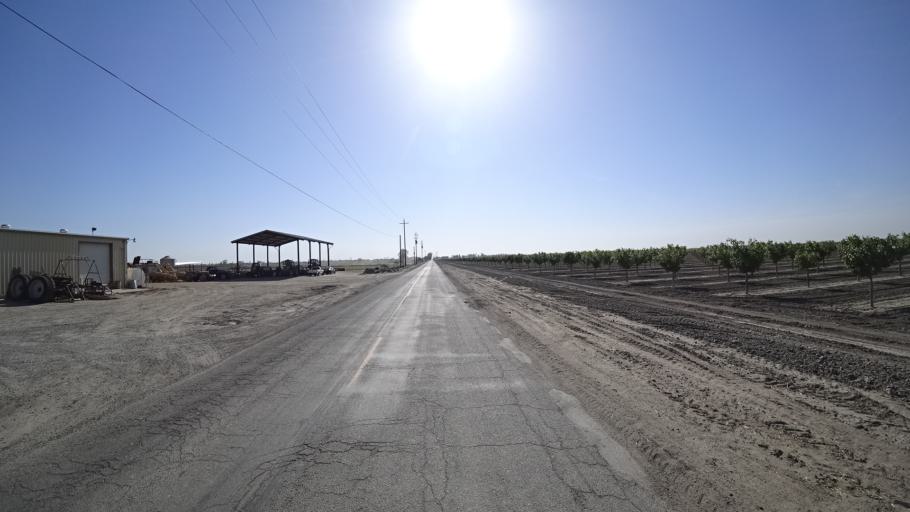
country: US
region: California
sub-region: Kings County
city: Corcoran
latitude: 36.0835
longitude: -119.5894
